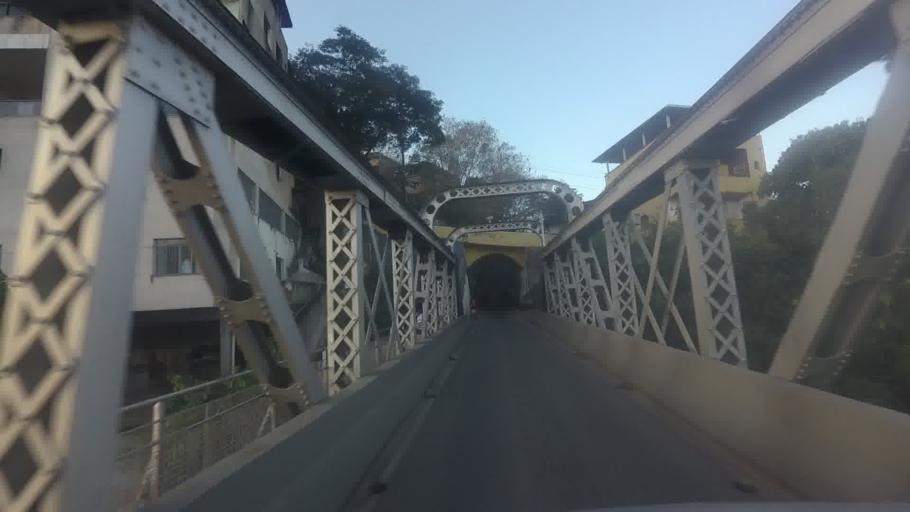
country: BR
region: Espirito Santo
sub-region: Cachoeiro De Itapemirim
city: Cachoeiro de Itapemirim
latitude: -20.8472
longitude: -41.1155
